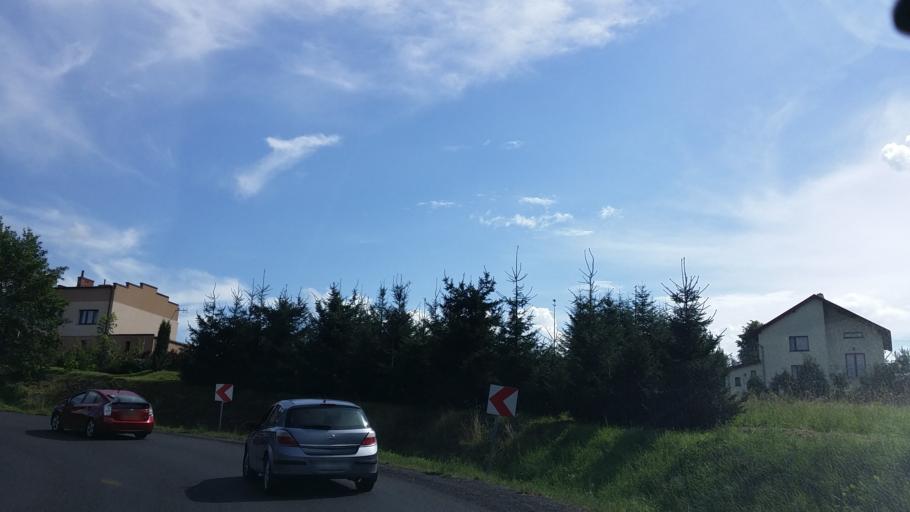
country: PL
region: Lesser Poland Voivodeship
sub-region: Powiat wielicki
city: Pawlikowice
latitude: 49.9375
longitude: 20.0542
